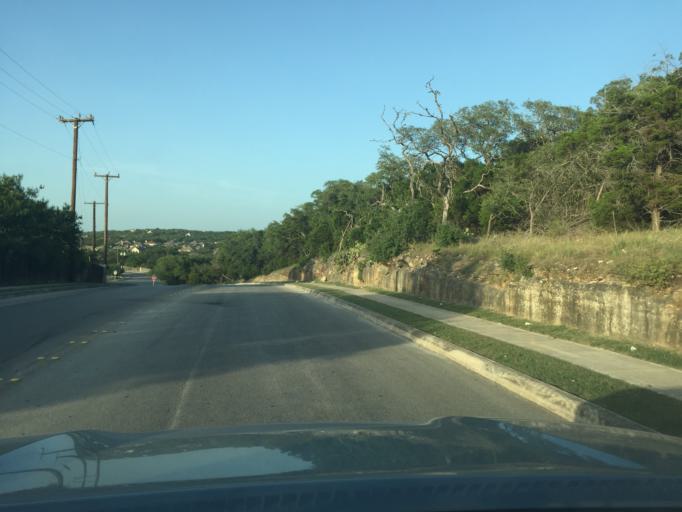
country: US
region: Texas
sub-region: Bexar County
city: Timberwood Park
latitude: 29.6869
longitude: -98.4781
